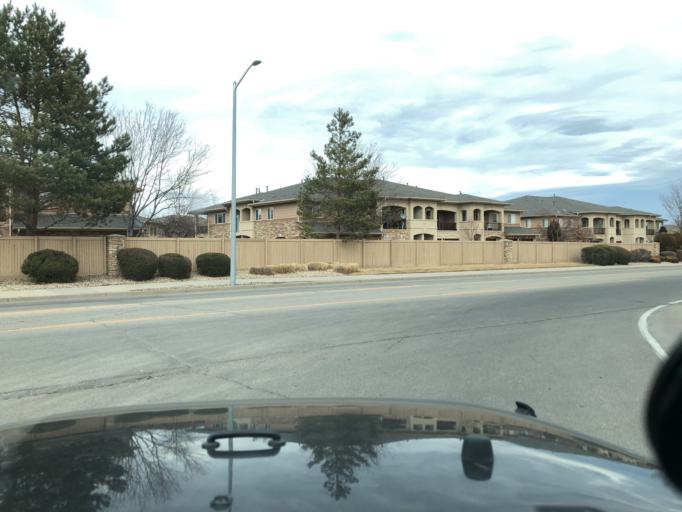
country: US
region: Colorado
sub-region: Boulder County
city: Longmont
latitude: 40.1885
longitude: -105.0760
